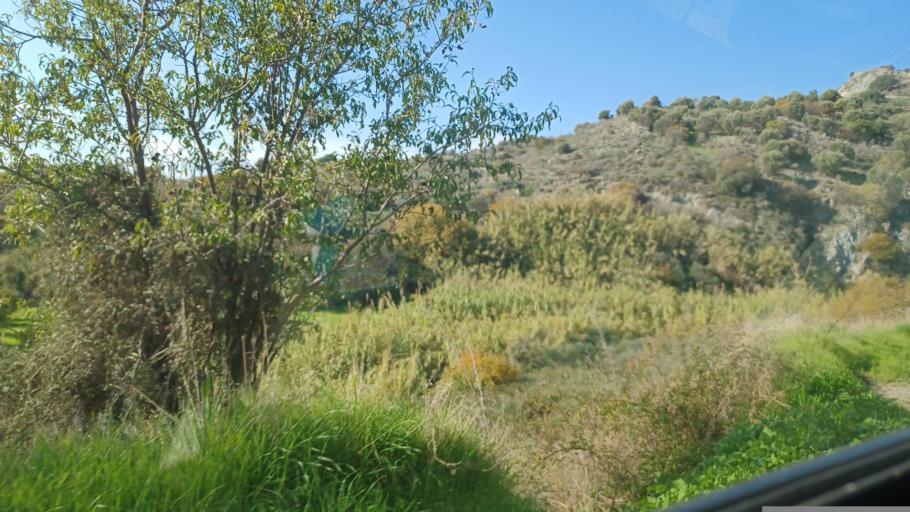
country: CY
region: Pafos
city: Mesogi
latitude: 34.7704
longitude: 32.5567
